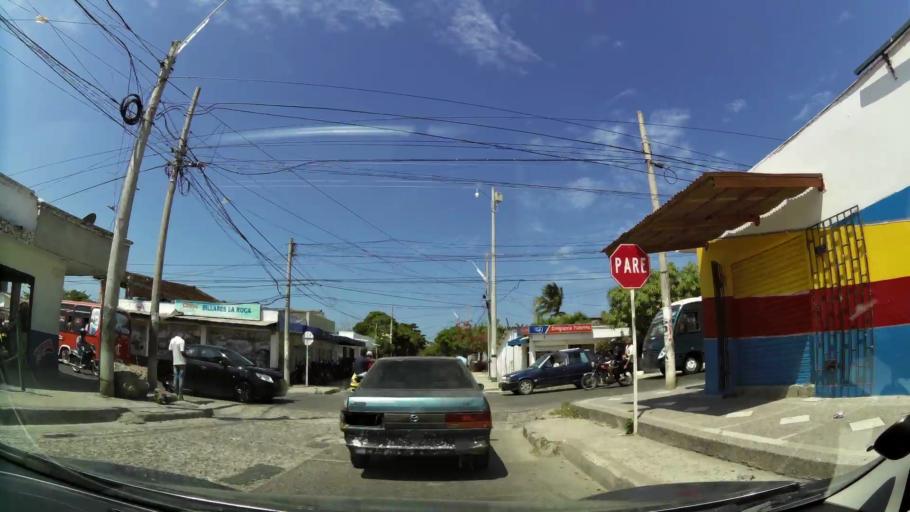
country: CO
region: Atlantico
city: Barranquilla
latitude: 10.9701
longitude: -74.8300
